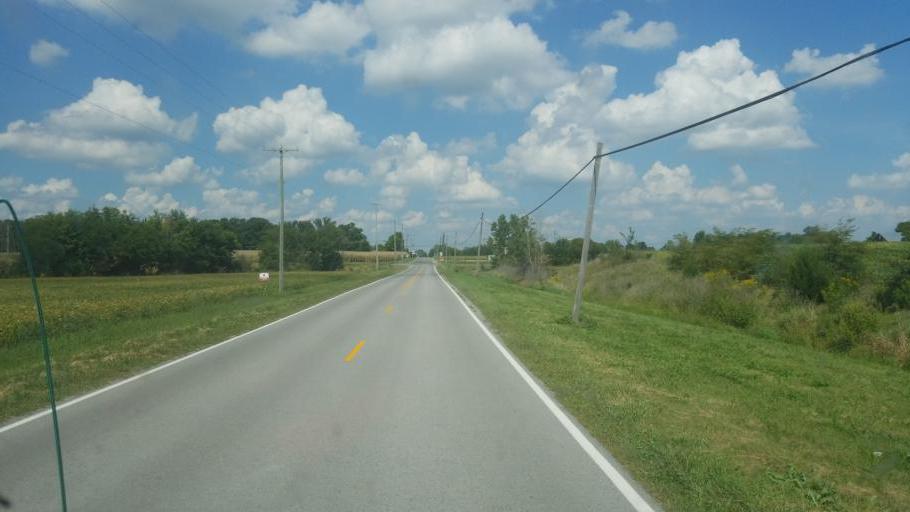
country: US
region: Ohio
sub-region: Hancock County
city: Arlington
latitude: 40.8903
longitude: -83.7271
